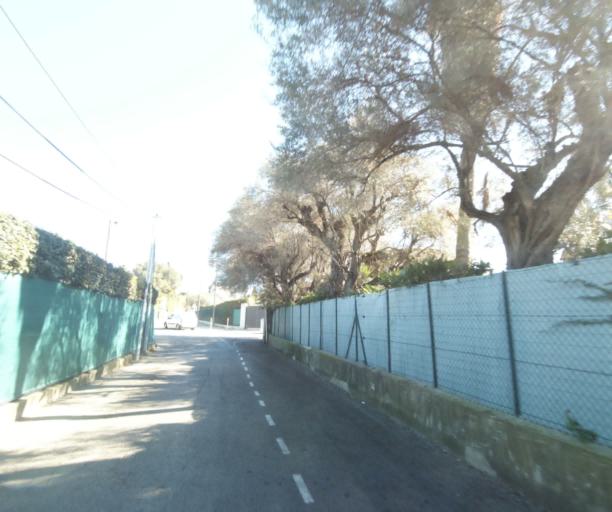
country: FR
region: Provence-Alpes-Cote d'Azur
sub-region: Departement des Alpes-Maritimes
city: Antibes
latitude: 43.5547
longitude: 7.1248
